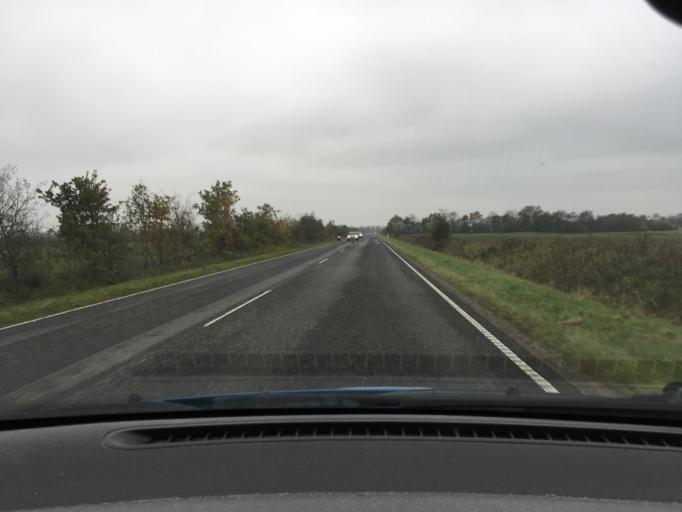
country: DK
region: South Denmark
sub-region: Aabenraa Kommune
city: Rodekro
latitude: 55.0699
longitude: 9.1743
